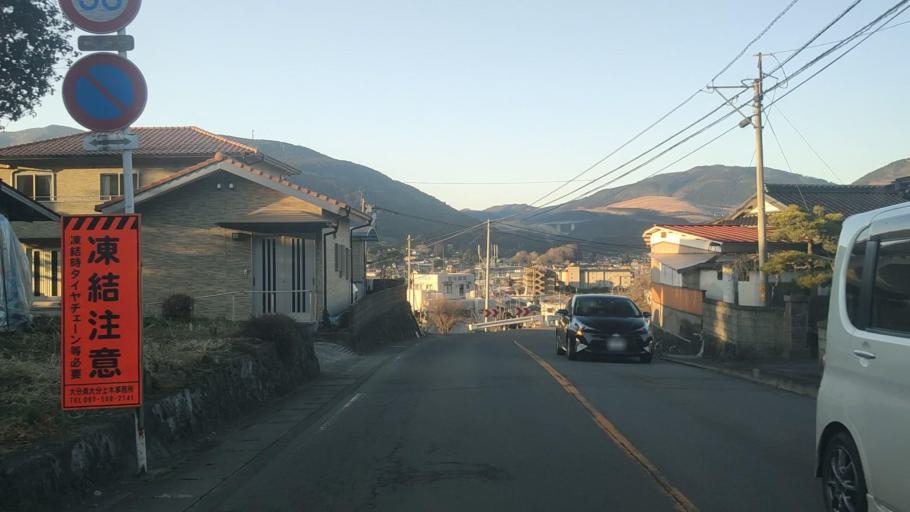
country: JP
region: Oita
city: Beppu
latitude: 33.2548
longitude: 131.3586
